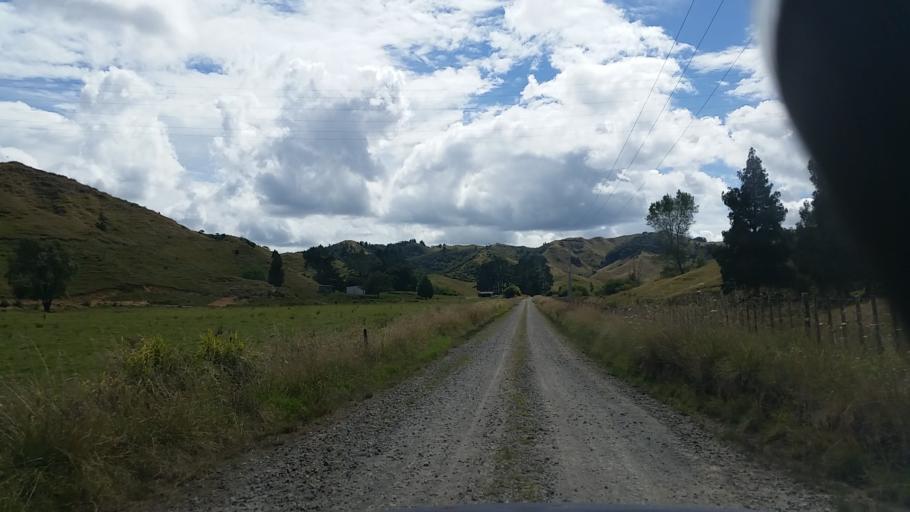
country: NZ
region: Taranaki
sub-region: South Taranaki District
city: Eltham
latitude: -39.2328
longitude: 174.5676
